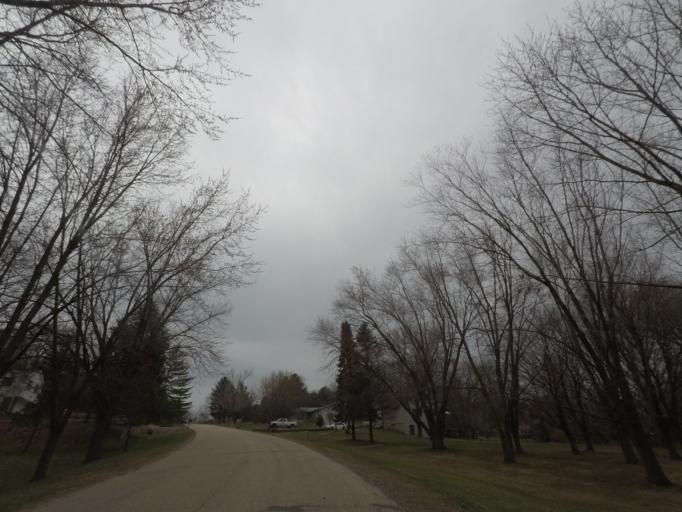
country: US
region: Wisconsin
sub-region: Dane County
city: Middleton
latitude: 43.1085
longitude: -89.5477
